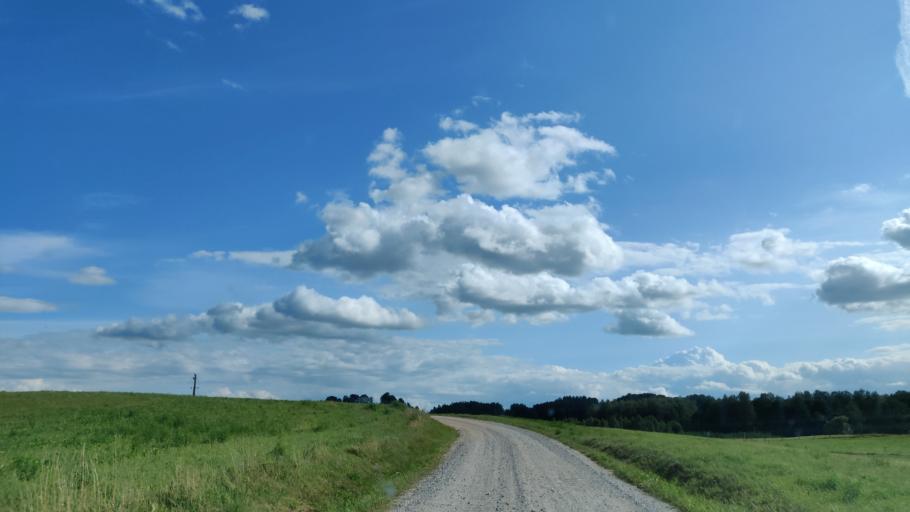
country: LT
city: Varniai
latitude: 55.6053
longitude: 22.3213
